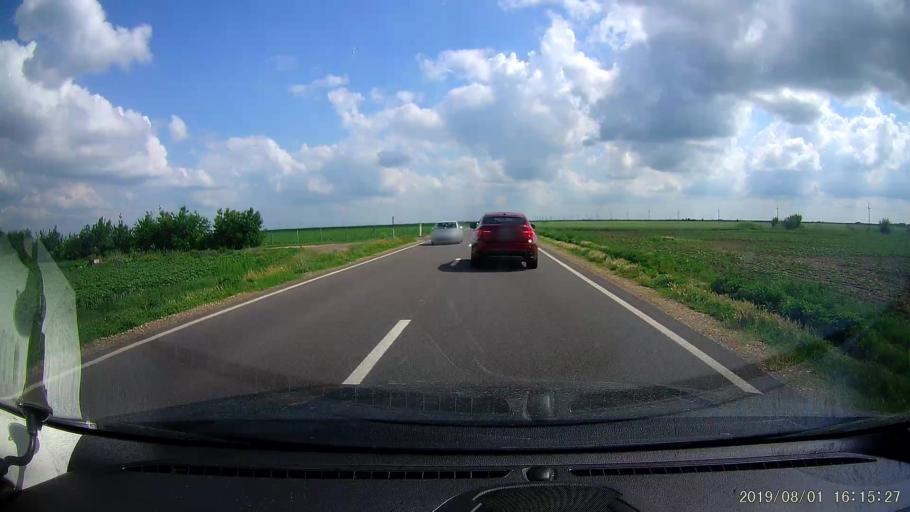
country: RO
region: Calarasi
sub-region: Comuna Stefan Voda
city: Stefan Voda
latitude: 44.3378
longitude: 27.3611
